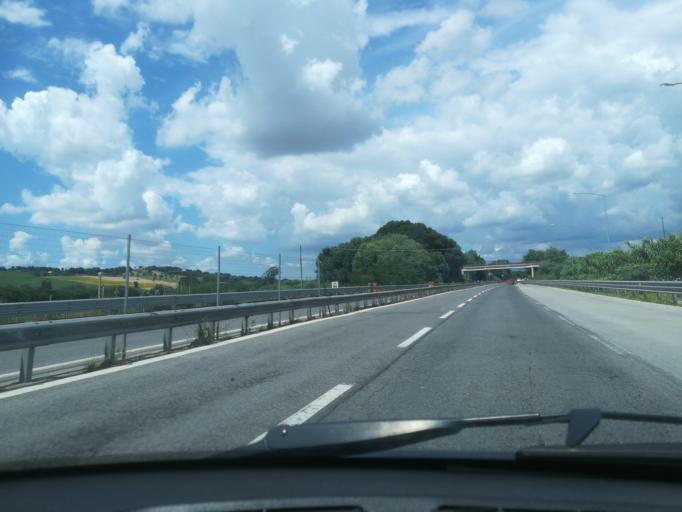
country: IT
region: The Marches
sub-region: Provincia di Macerata
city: Villa San Filippo
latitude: 43.2629
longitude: 13.5594
